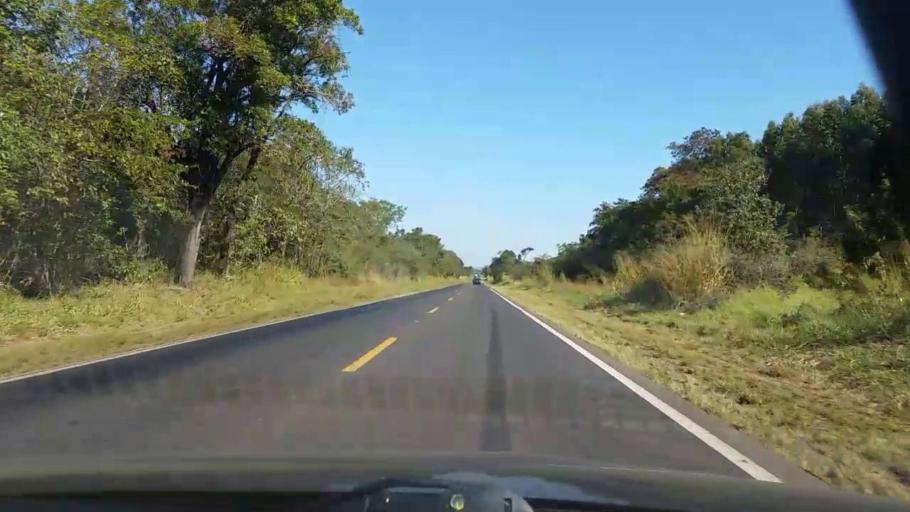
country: BR
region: Sao Paulo
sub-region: Sao Manuel
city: Sao Manuel
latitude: -22.8947
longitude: -48.7632
